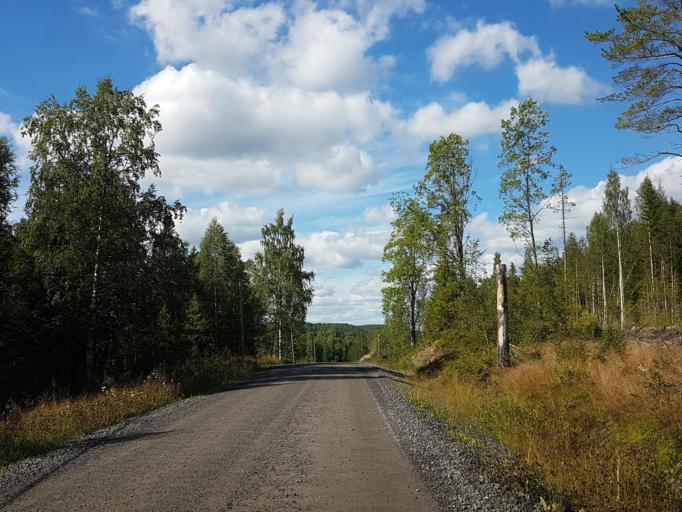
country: SE
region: Vaesterbotten
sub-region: Skelleftea Kommun
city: Burtraesk
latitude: 64.2859
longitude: 20.4600
